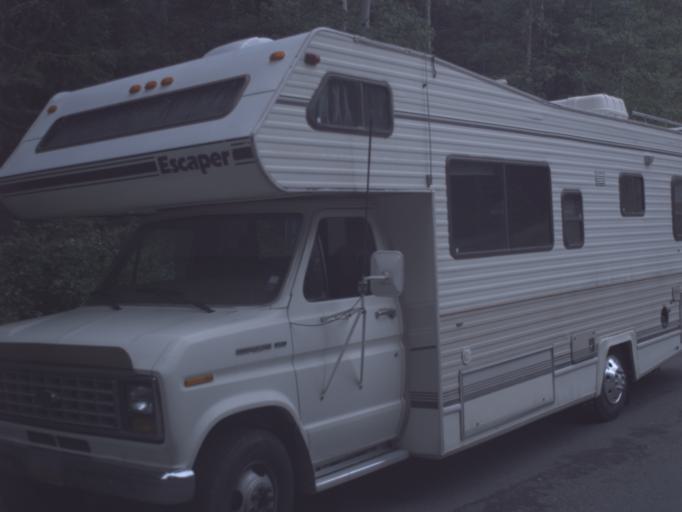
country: US
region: Utah
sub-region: Utah County
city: Lindon
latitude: 40.4330
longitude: -111.6361
